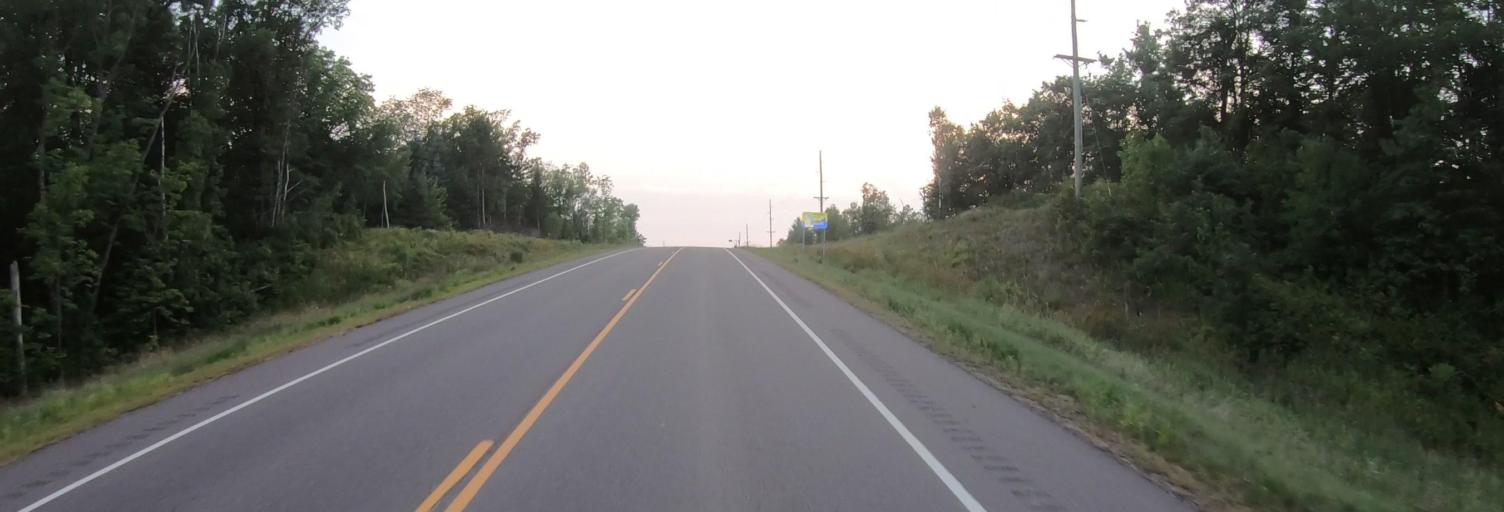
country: US
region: Wisconsin
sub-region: Burnett County
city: Grantsburg
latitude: 45.7734
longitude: -92.7860
